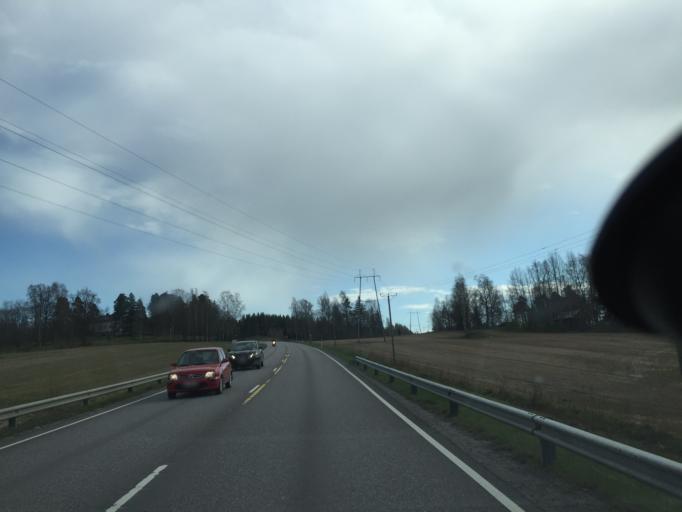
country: FI
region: Uusimaa
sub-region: Raaseporin
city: Ekenaes
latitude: 60.0485
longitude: 23.3321
